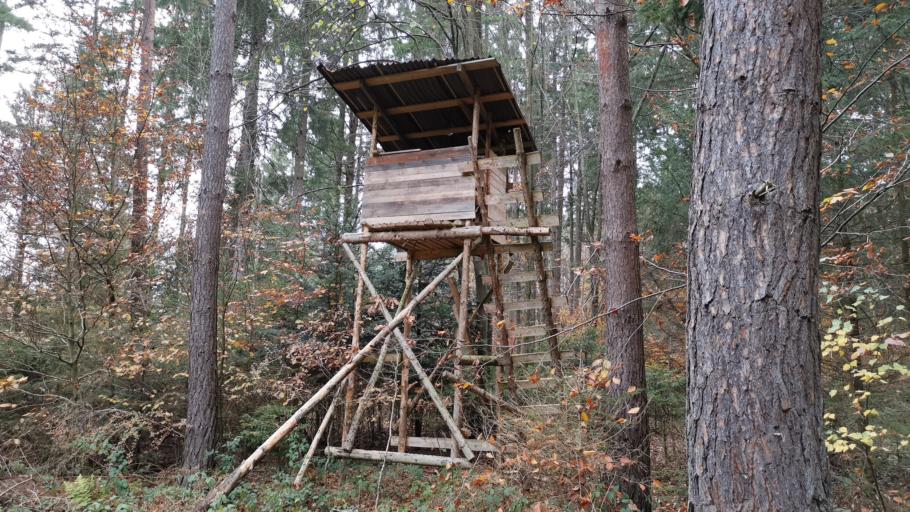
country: DE
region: Bavaria
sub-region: Upper Bavaria
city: Planegg
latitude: 48.0878
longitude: 11.4275
